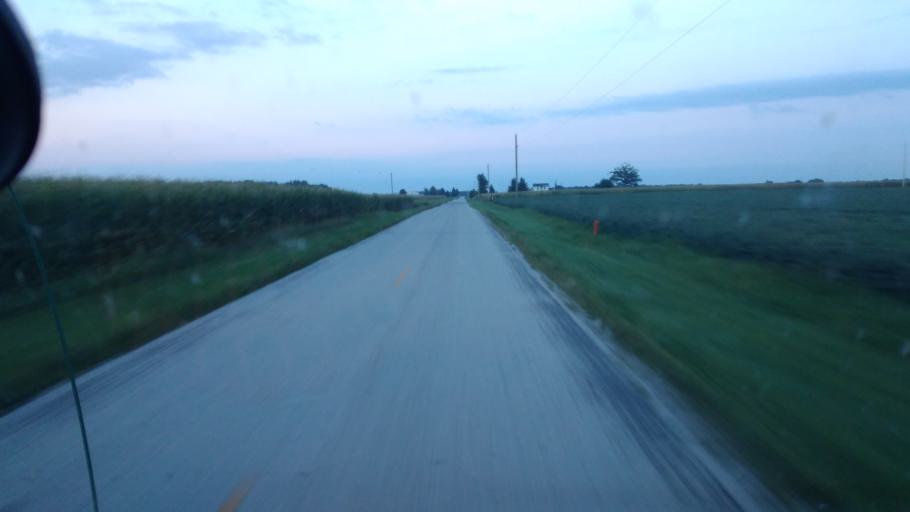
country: US
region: Ohio
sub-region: Hardin County
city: Forest
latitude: 40.6727
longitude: -83.4616
